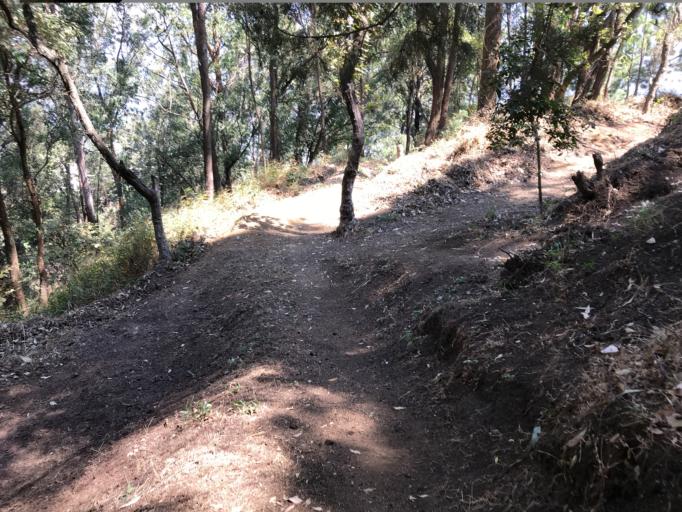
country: GT
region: Guatemala
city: Villa Canales
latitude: 14.4793
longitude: -90.5462
